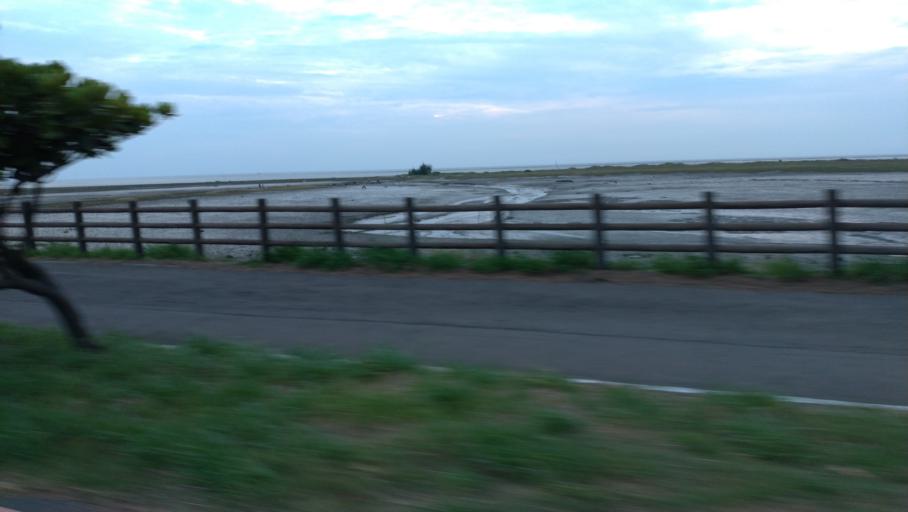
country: TW
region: Taiwan
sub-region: Hsinchu
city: Hsinchu
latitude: 24.7579
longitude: 120.9061
